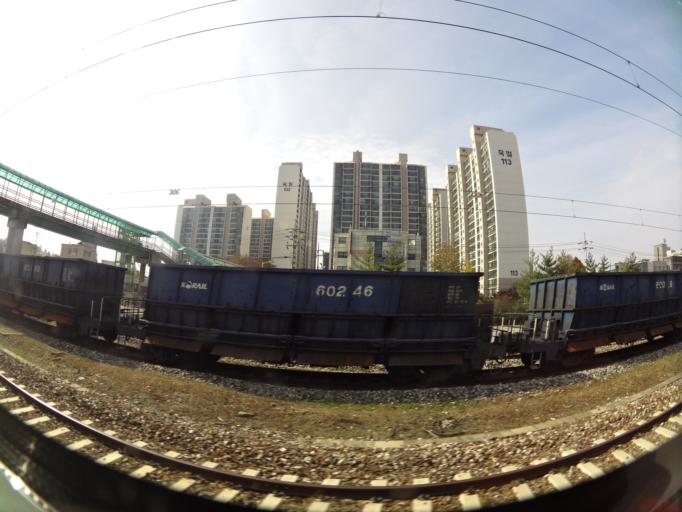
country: KR
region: Daejeon
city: Songgang-dong
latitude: 36.6028
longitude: 127.2952
